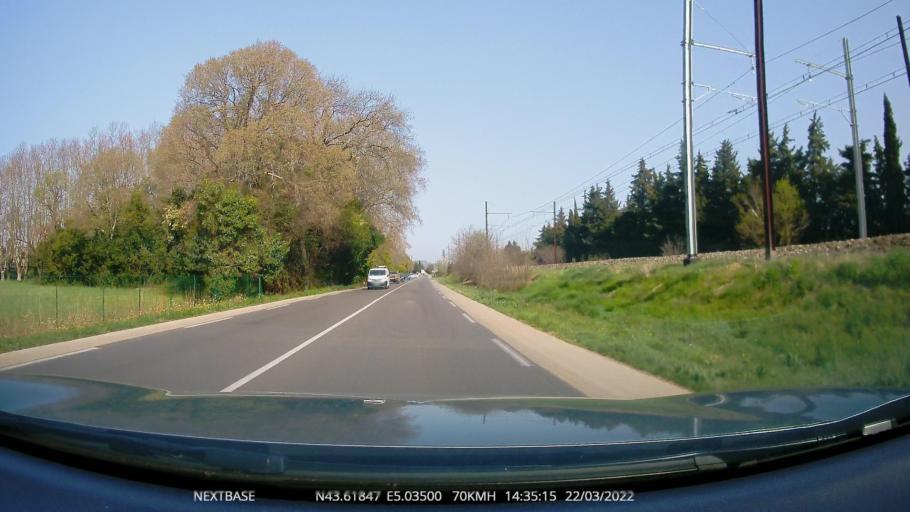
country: FR
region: Provence-Alpes-Cote d'Azur
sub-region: Departement des Bouches-du-Rhone
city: Grans
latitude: 43.6185
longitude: 5.0351
